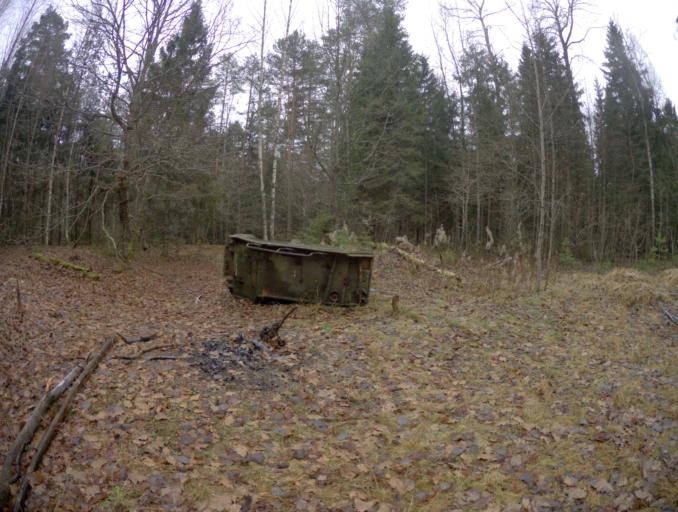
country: RU
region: Vladimir
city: Golovino
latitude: 56.0148
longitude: 40.4979
